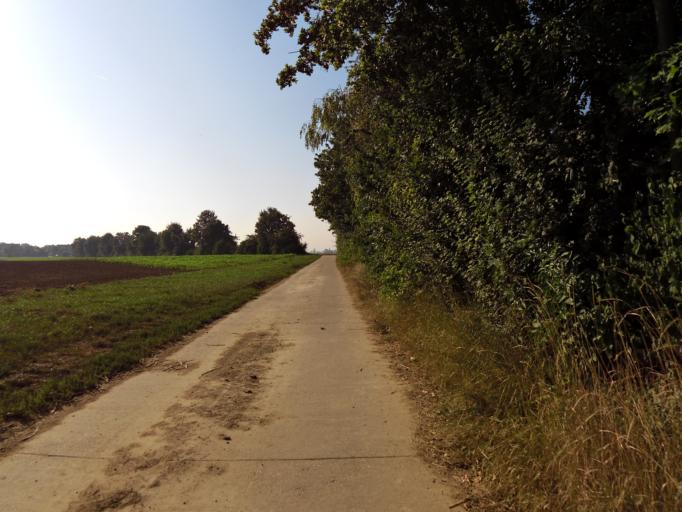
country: DE
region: Rheinland-Pfalz
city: Kleinniedesheim
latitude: 49.5930
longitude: 8.3157
